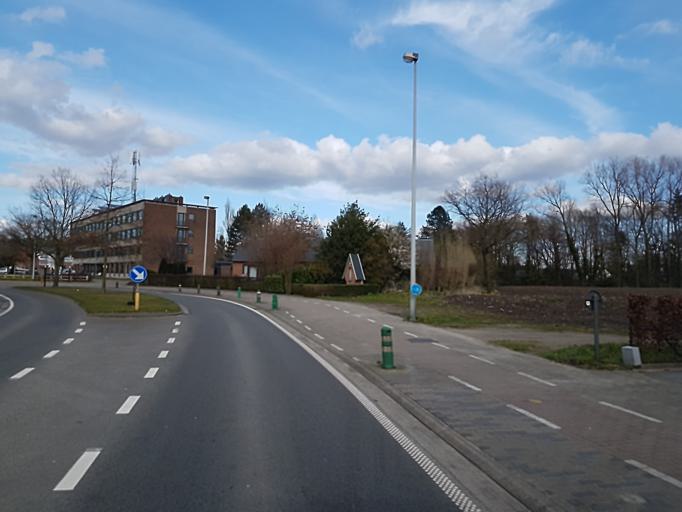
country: BE
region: Flanders
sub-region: Provincie Oost-Vlaanderen
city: Sint-Niklaas
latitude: 51.1916
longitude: 4.1722
